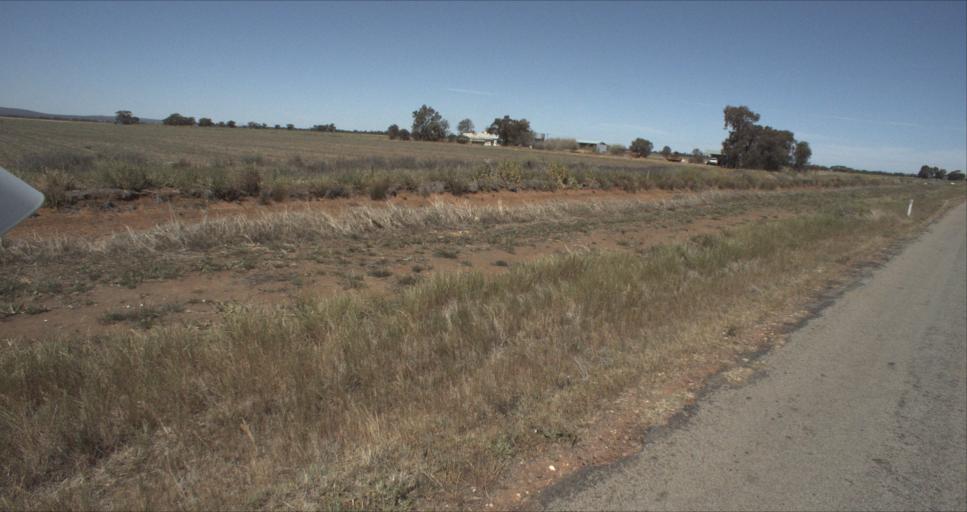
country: AU
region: New South Wales
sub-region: Leeton
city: Leeton
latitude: -34.5028
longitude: 146.3442
